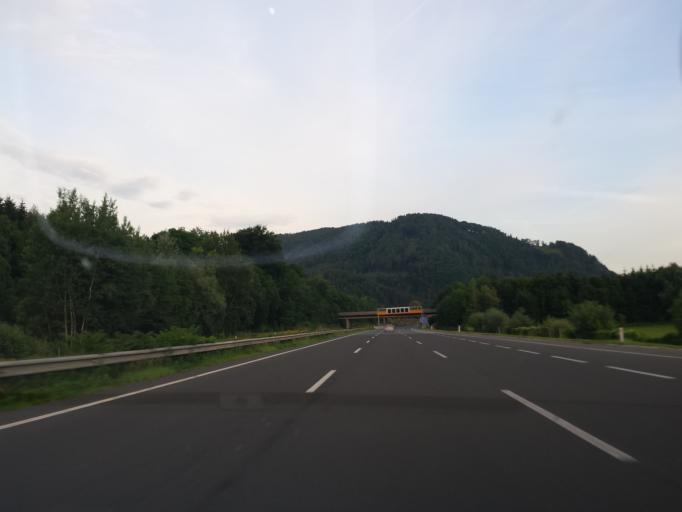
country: AT
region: Styria
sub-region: Politischer Bezirk Graz-Umgebung
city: Deutschfeistritz
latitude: 47.1737
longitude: 15.3319
